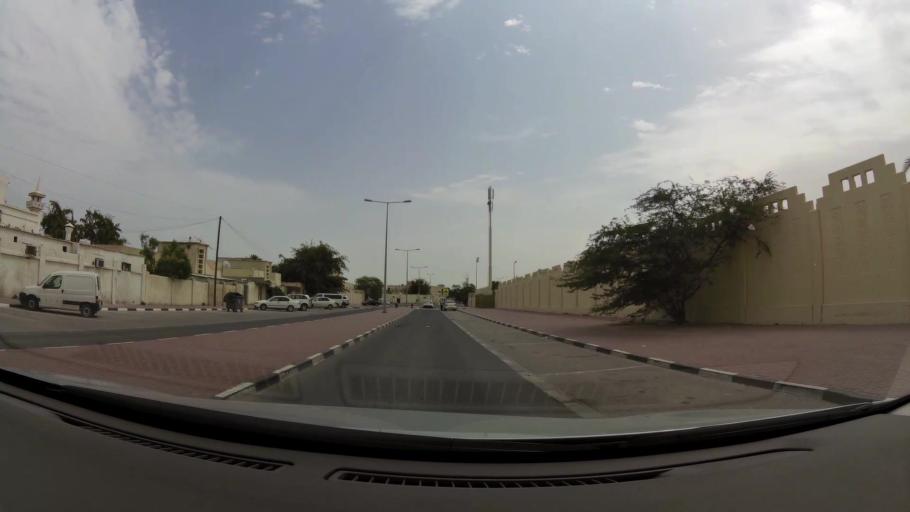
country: QA
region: Baladiyat ar Rayyan
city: Ar Rayyan
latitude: 25.3332
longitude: 51.4702
